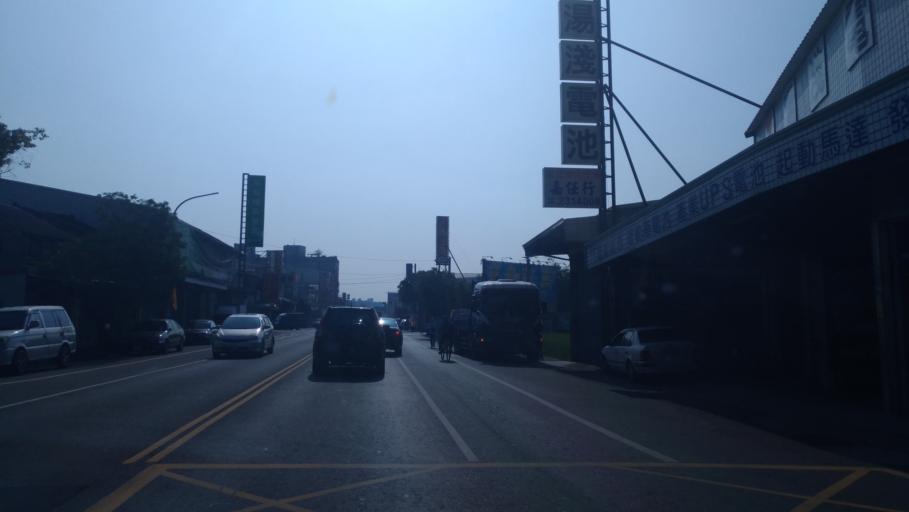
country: TW
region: Taiwan
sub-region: Chiayi
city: Jiayi Shi
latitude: 23.4986
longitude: 120.4417
